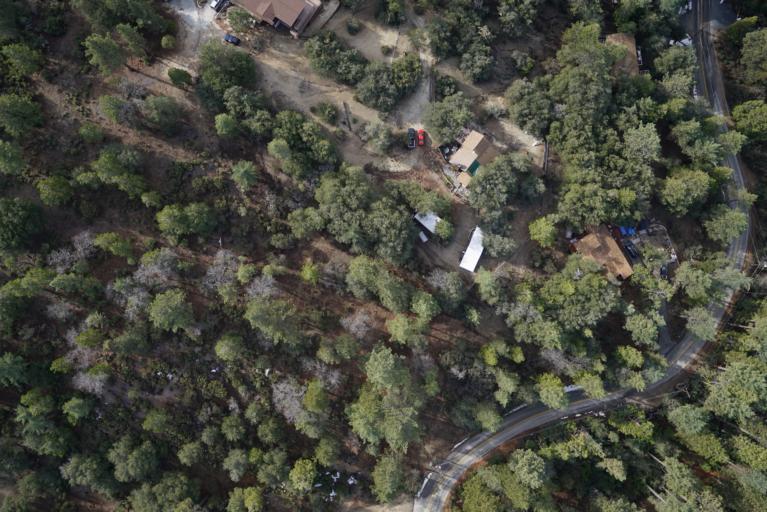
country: US
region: California
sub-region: Riverside County
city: Idyllwild
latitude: 33.7293
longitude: -116.7132
